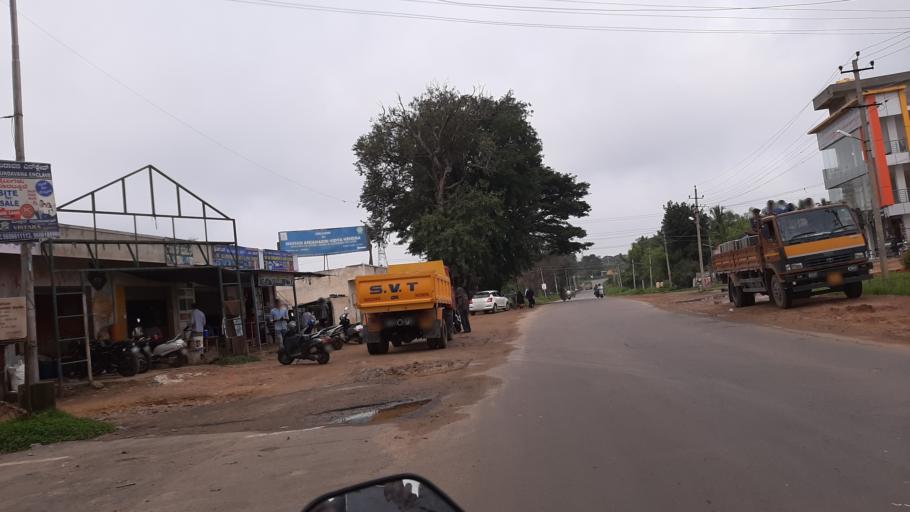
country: IN
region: Karnataka
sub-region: Bangalore Rural
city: Nelamangala
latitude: 12.9650
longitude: 77.3950
